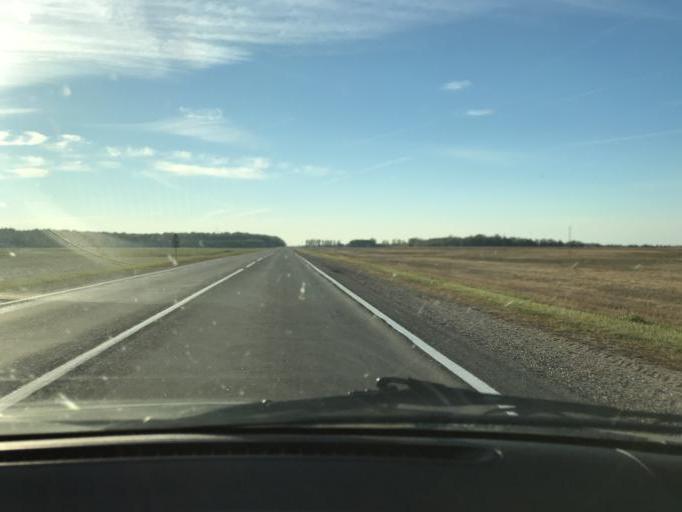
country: BY
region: Brest
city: Antopal'
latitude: 52.2271
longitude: 24.7805
